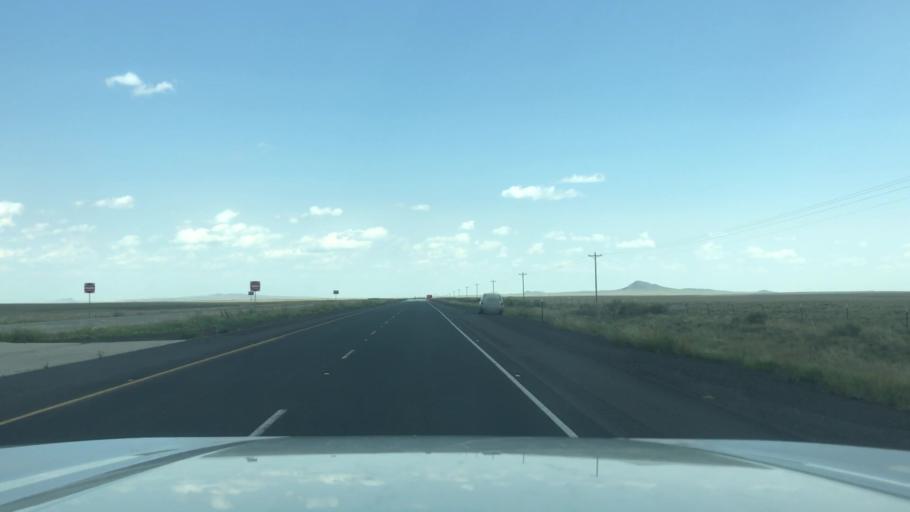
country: US
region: New Mexico
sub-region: Union County
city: Clayton
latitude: 36.6326
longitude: -103.7162
